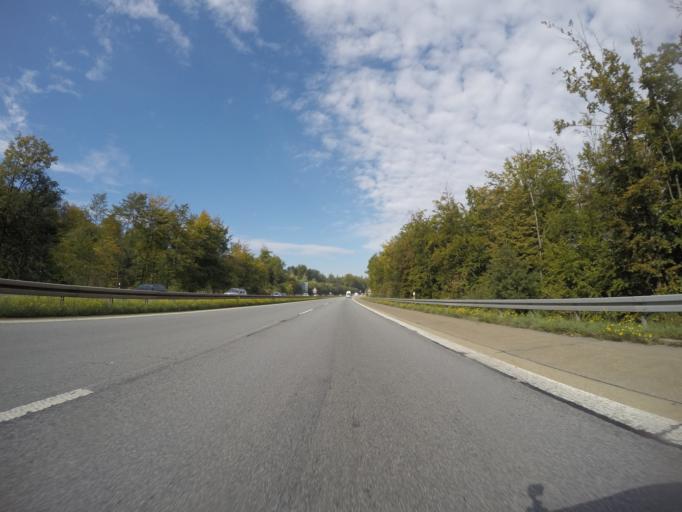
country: DE
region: Bavaria
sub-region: Regierungsbezirk Unterfranken
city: Weibersbrunn
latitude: 49.9045
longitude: 9.3768
